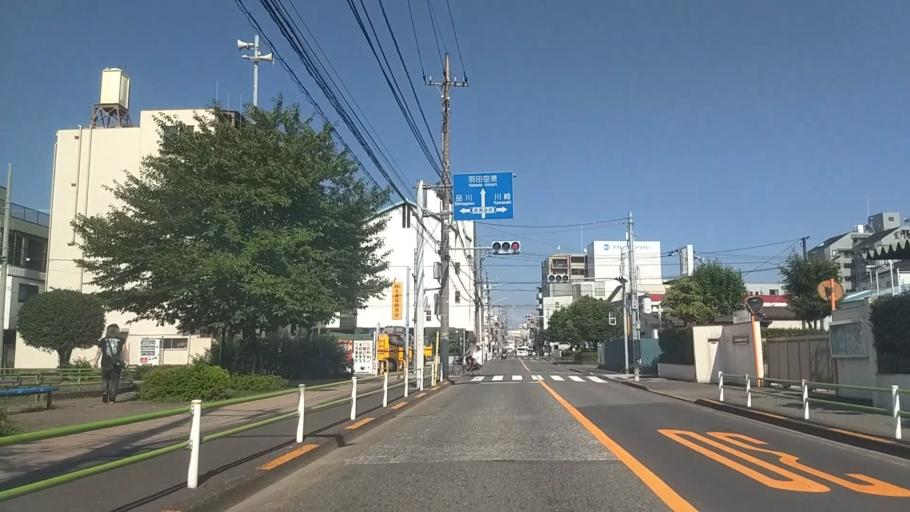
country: JP
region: Kanagawa
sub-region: Kawasaki-shi
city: Kawasaki
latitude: 35.5492
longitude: 139.7396
